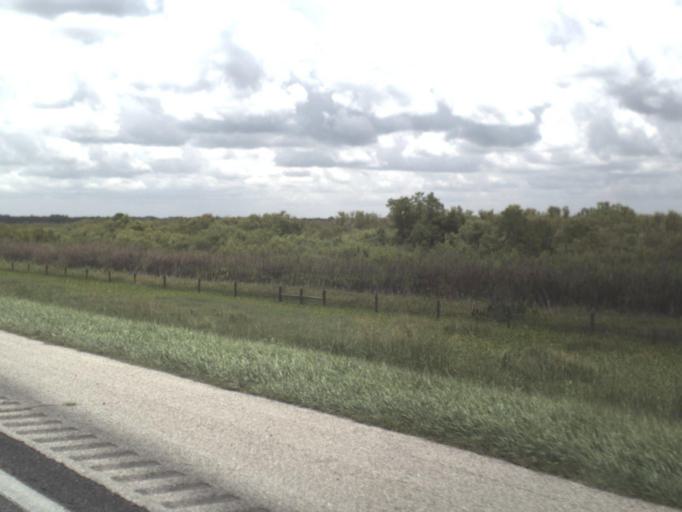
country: US
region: Florida
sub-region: Alachua County
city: Gainesville
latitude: 29.5775
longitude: -82.3555
